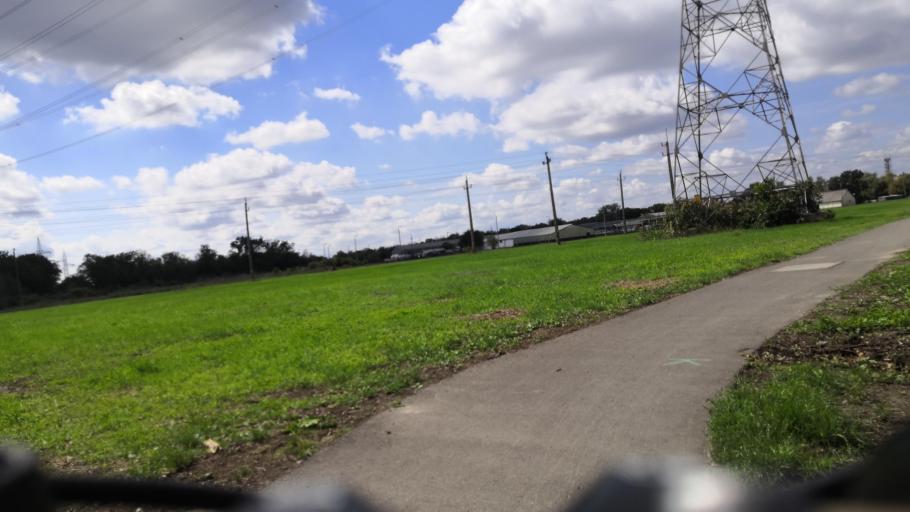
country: HU
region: Csongrad
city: Szeged
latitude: 46.2778
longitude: 20.1347
